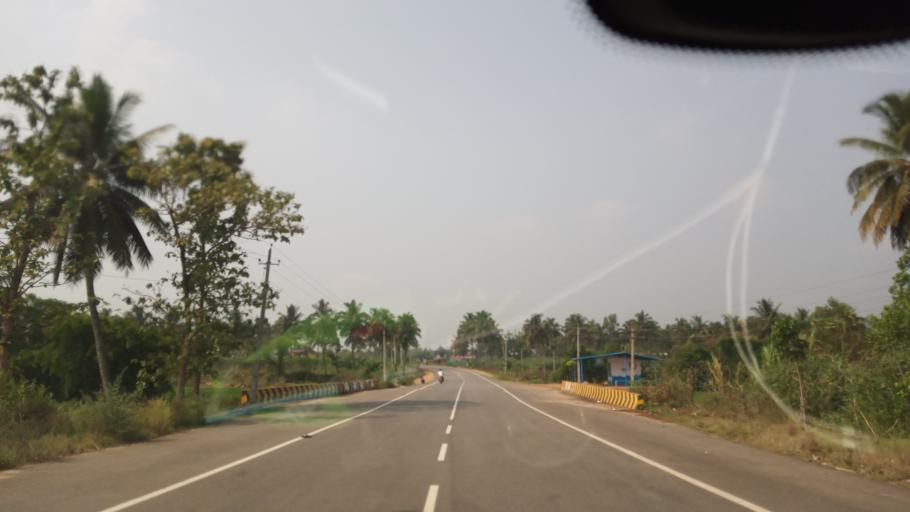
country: IN
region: Karnataka
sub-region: Mandya
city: Pandavapura
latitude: 12.5422
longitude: 76.6706
